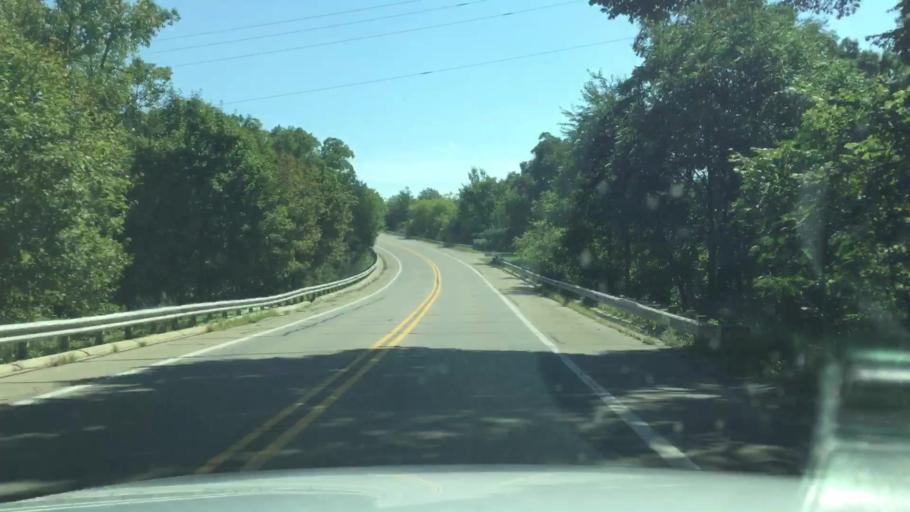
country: US
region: Michigan
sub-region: Jackson County
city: Brooklyn
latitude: 42.0585
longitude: -84.1769
